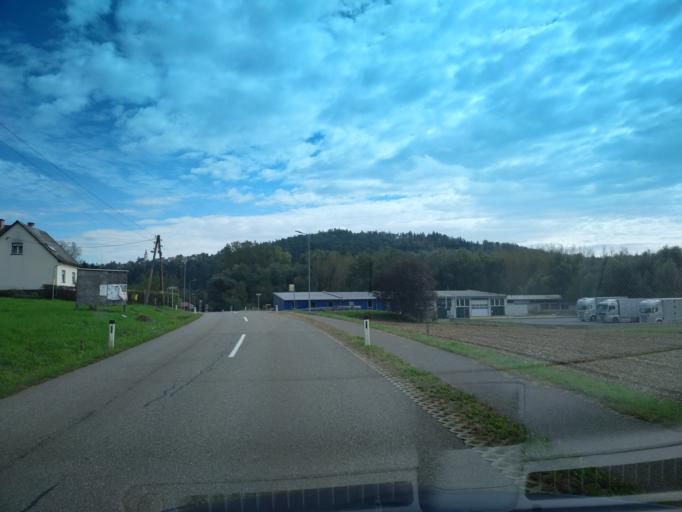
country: AT
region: Styria
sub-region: Politischer Bezirk Leibnitz
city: Seggauberg
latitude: 46.7761
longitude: 15.5052
